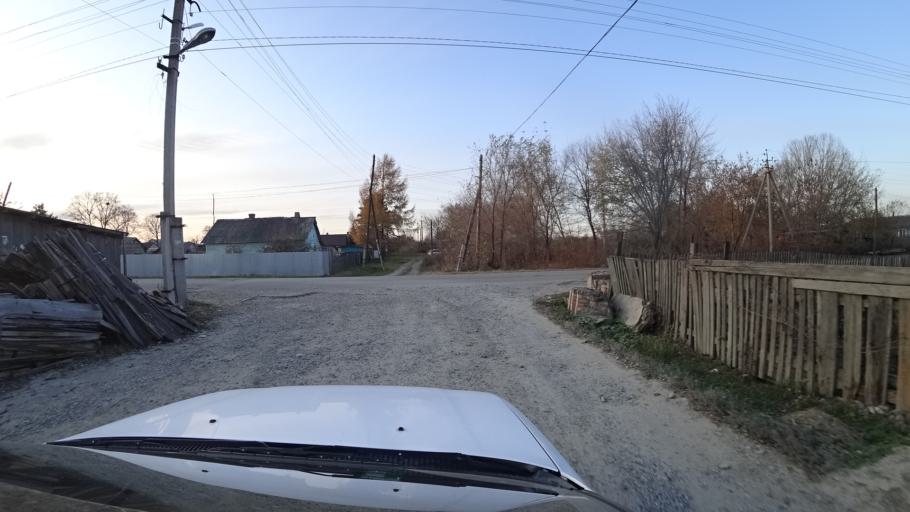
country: RU
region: Primorskiy
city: Dal'nerechensk
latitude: 45.9477
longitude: 133.8207
